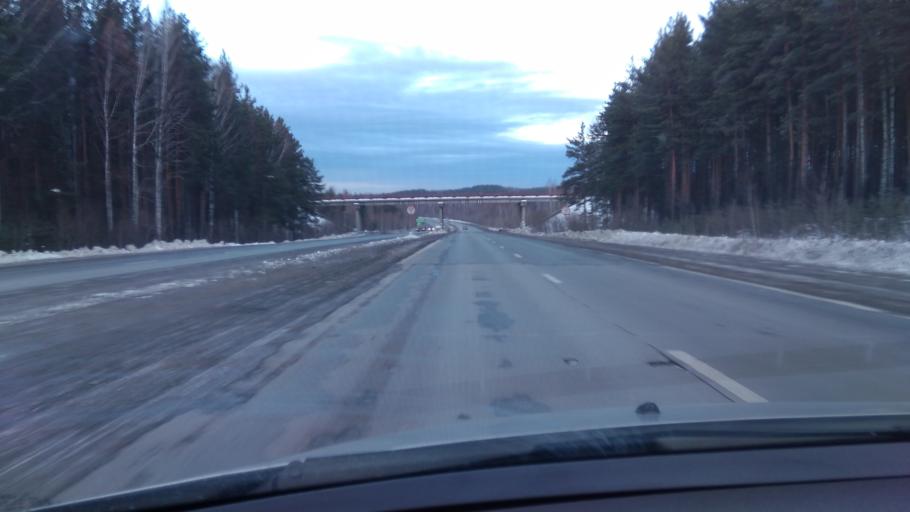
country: RU
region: Sverdlovsk
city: Shchelkun
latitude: 56.3165
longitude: 60.8692
